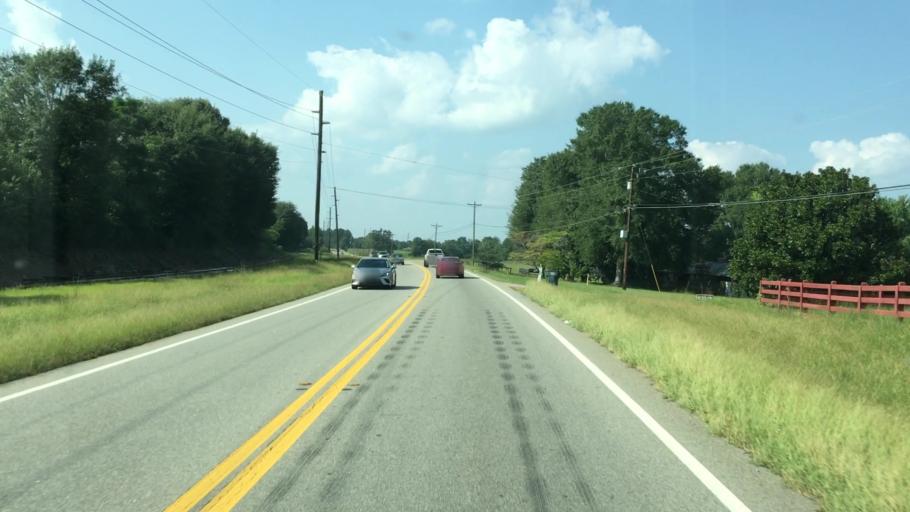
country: US
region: Georgia
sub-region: Walton County
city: Social Circle
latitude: 33.6980
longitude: -83.7014
